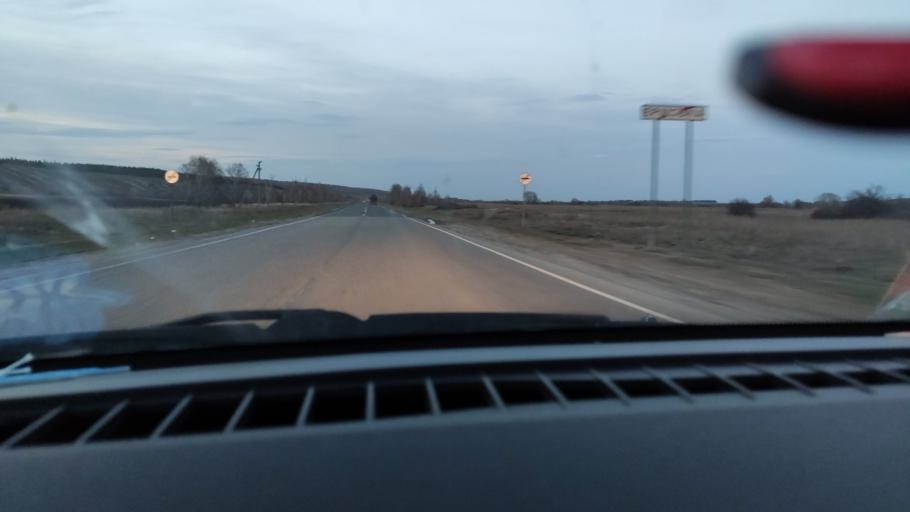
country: RU
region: Saratov
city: Sinodskoye
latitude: 52.0554
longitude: 46.7575
